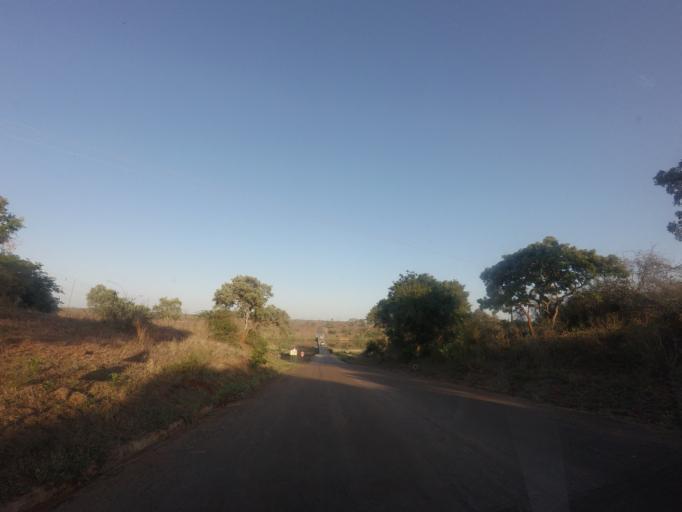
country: ZA
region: Mpumalanga
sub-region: Ehlanzeni District
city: Komatipoort
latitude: -25.3632
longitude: 31.8956
